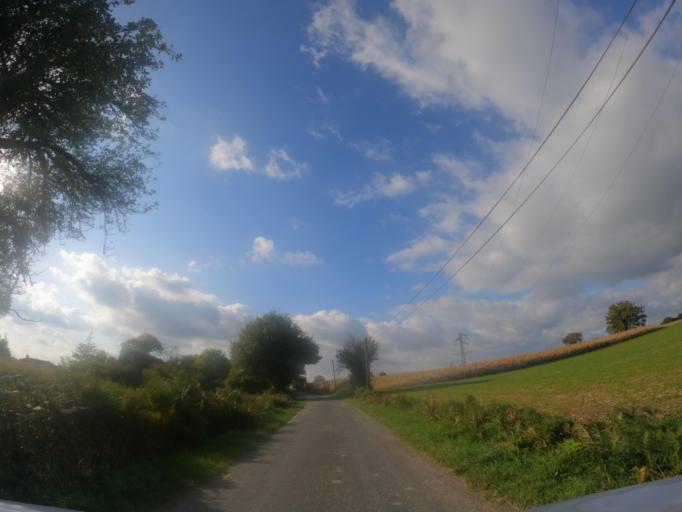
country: FR
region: Poitou-Charentes
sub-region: Departement des Deux-Sevres
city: La Foret-sur-Sevre
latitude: 46.7832
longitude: -0.6202
